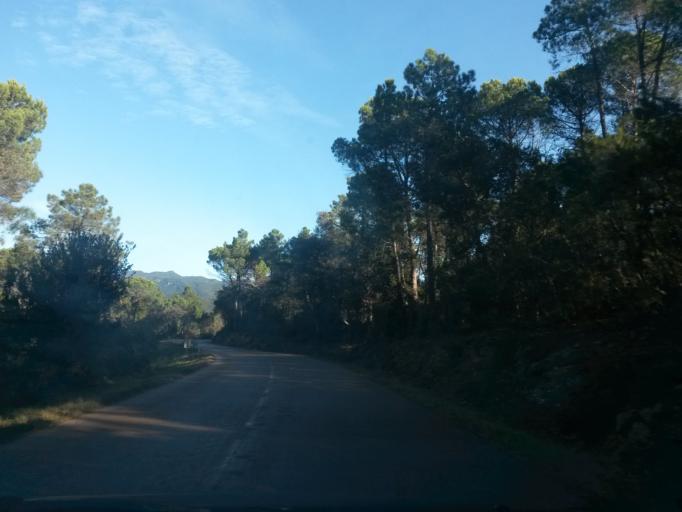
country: ES
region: Catalonia
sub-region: Provincia de Girona
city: la Cellera de Ter
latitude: 42.0090
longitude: 2.6730
